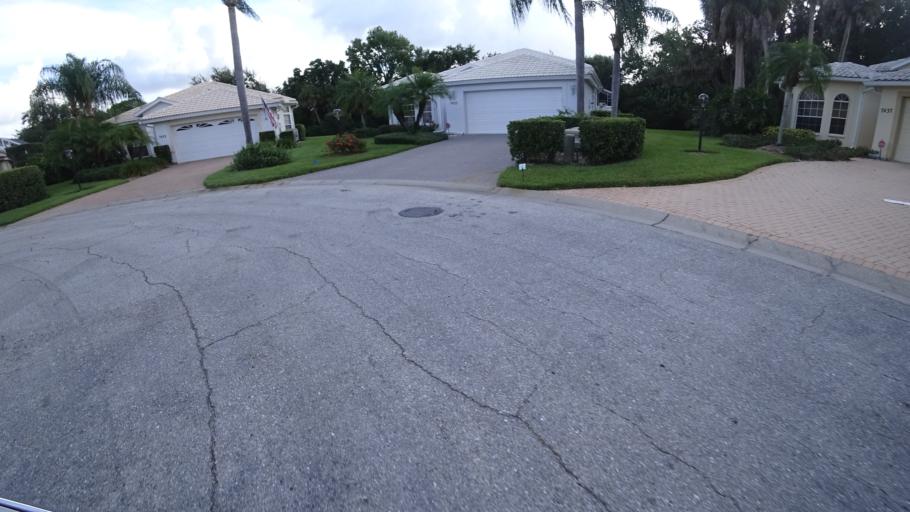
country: US
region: Florida
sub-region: Sarasota County
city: Desoto Lakes
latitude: 27.4073
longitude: -82.4854
